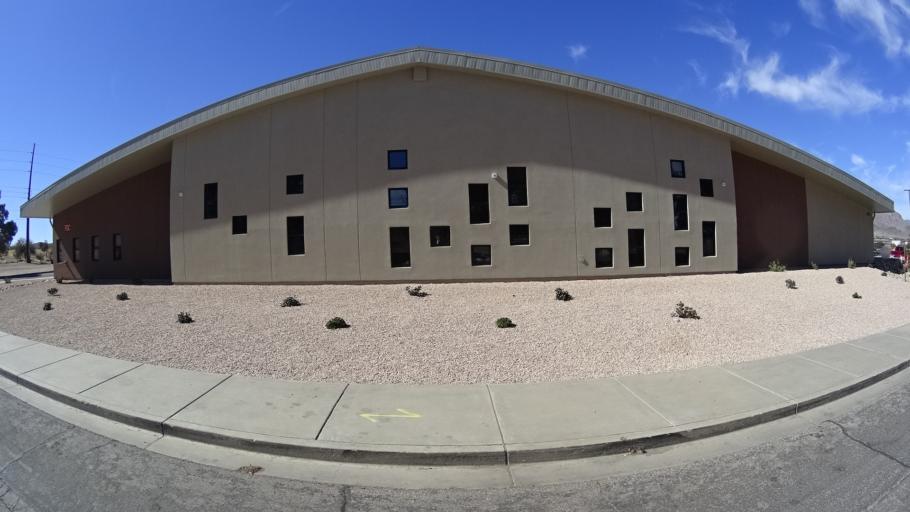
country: US
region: Arizona
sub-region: Mohave County
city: Kingman
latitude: 35.2190
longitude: -114.0292
